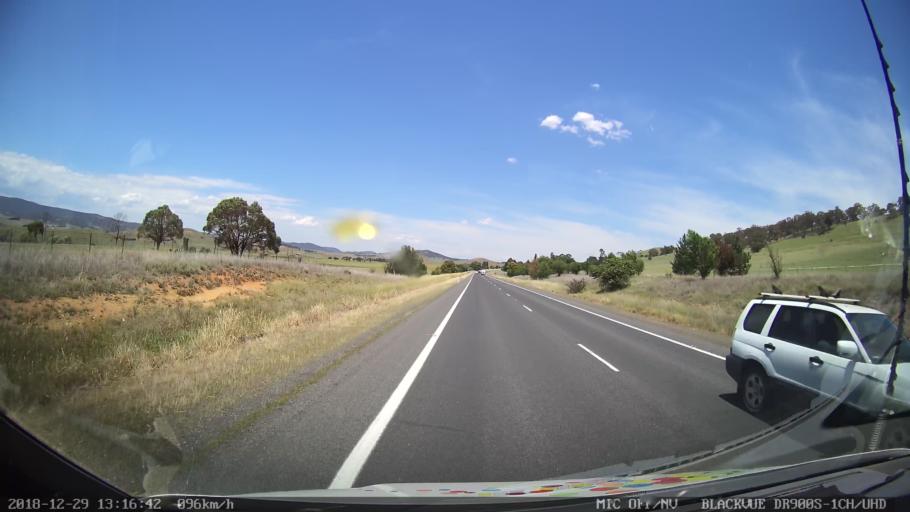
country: AU
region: Australian Capital Territory
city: Macarthur
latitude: -35.7270
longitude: 149.1599
